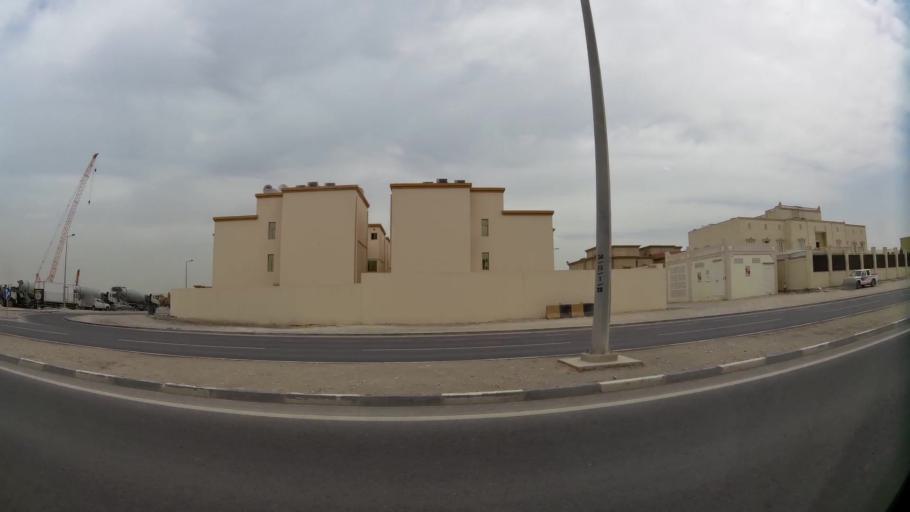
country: QA
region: Baladiyat ad Dawhah
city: Doha
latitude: 25.2283
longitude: 51.4701
